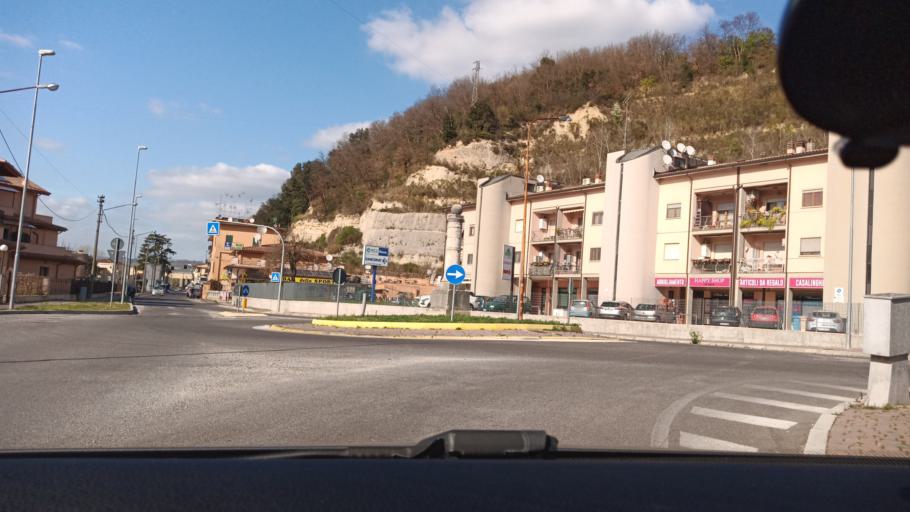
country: IT
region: Latium
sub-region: Citta metropolitana di Roma Capitale
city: Torrita Tiberina
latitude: 42.2396
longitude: 12.6340
